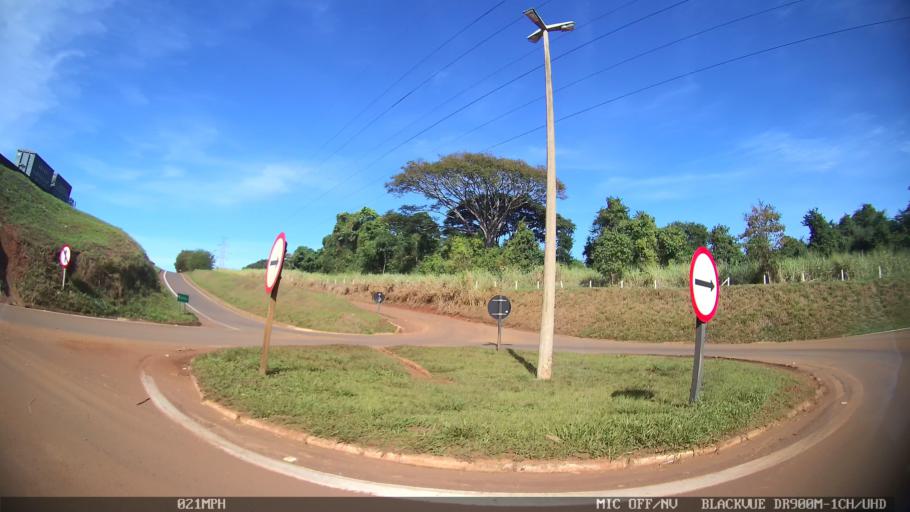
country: BR
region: Sao Paulo
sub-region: Araras
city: Araras
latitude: -22.3128
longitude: -47.3913
